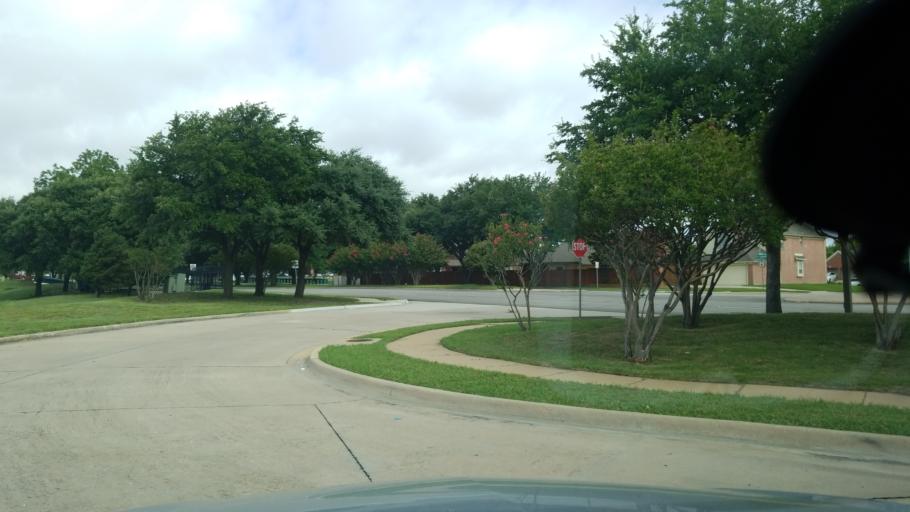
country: US
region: Texas
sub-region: Dallas County
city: Farmers Branch
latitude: 32.9431
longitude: -96.9500
